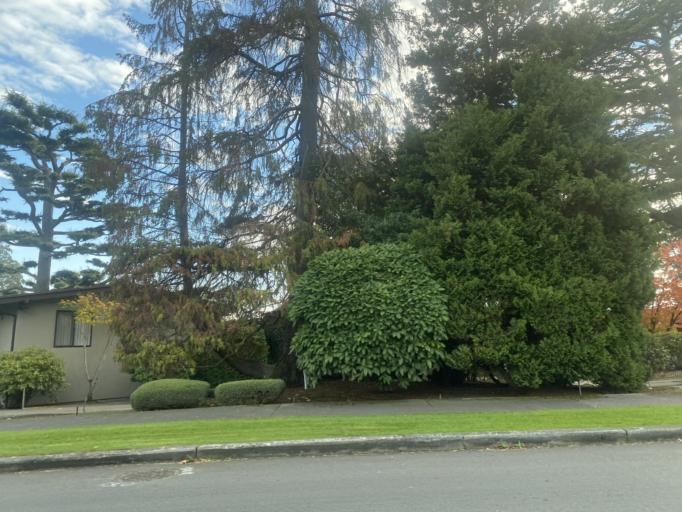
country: US
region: Washington
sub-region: King County
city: Seattle
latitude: 47.6370
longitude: -122.4051
